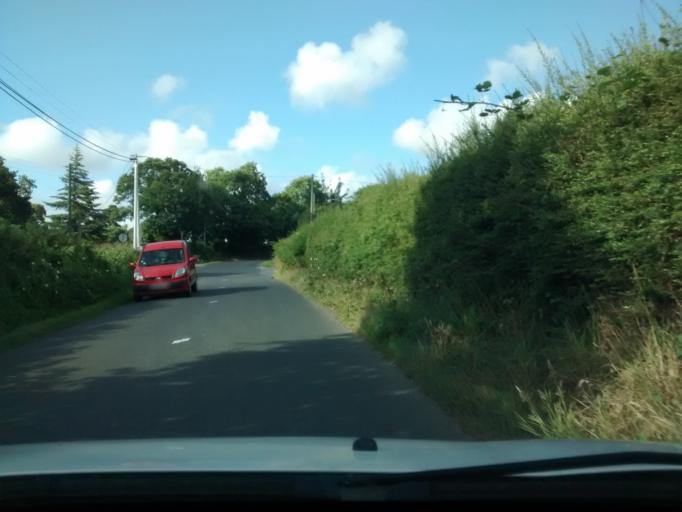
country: FR
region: Brittany
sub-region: Departement des Cotes-d'Armor
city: Lannion
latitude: 48.7431
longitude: -3.4271
